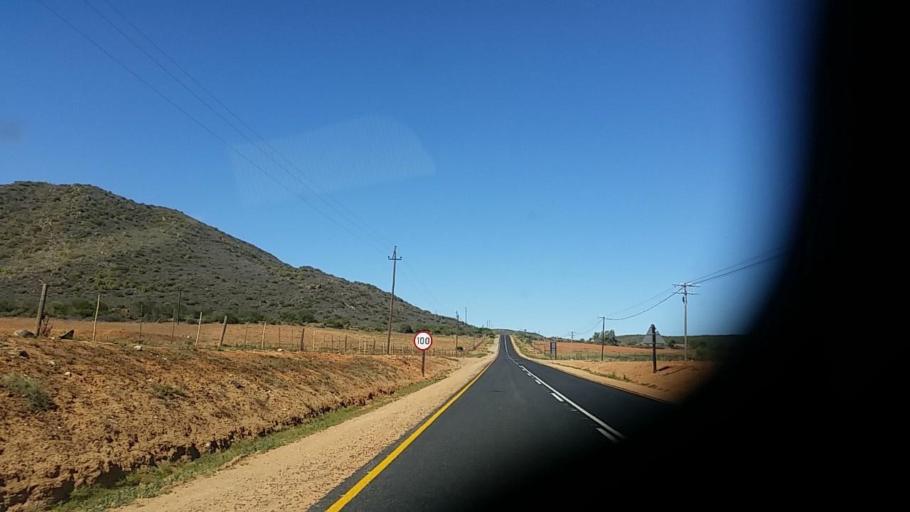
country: ZA
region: Western Cape
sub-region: Eden District Municipality
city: Oudtshoorn
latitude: -33.4865
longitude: 22.5446
